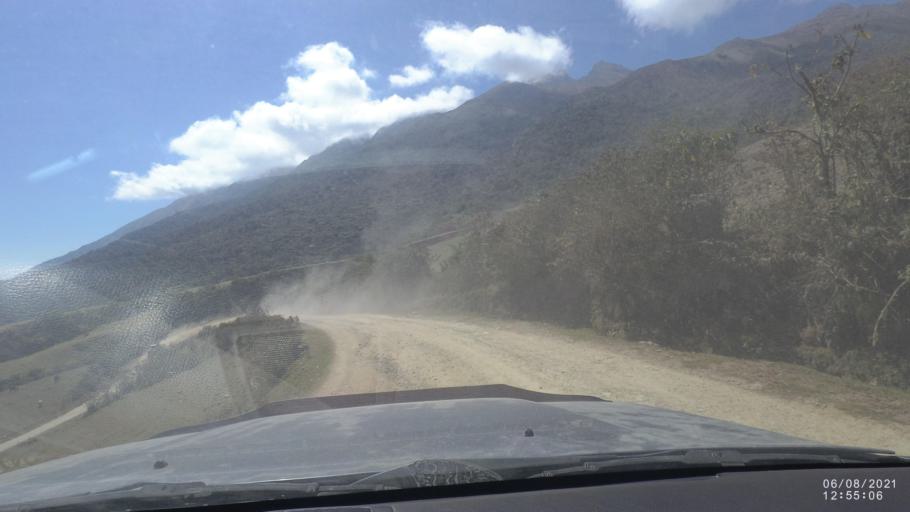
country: BO
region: Cochabamba
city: Colchani
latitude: -16.7557
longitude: -66.6819
